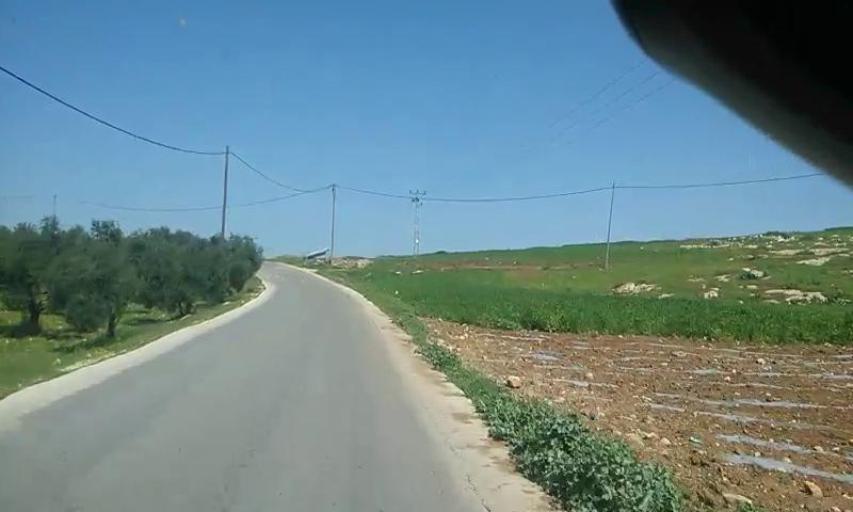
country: PS
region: West Bank
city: Al Majd
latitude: 31.4732
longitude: 34.9488
